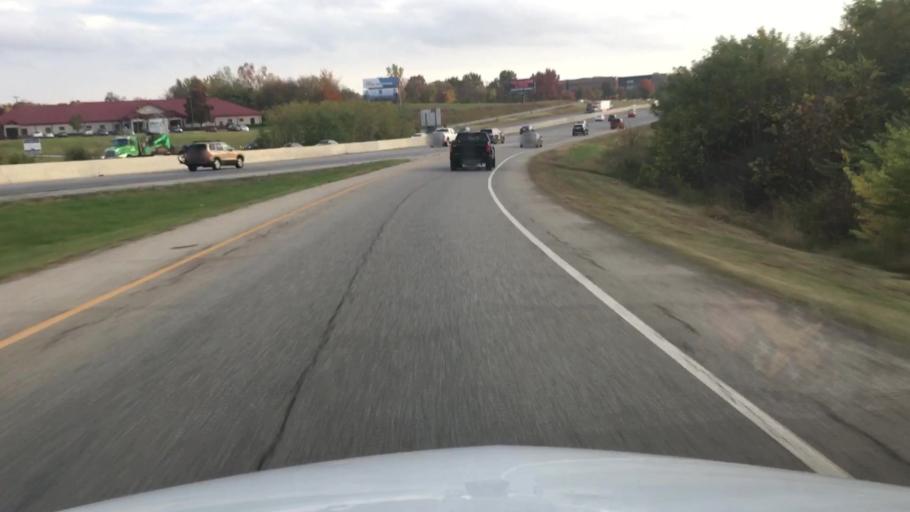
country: US
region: Arkansas
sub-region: Benton County
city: Lowell
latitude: 36.2514
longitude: -94.1509
